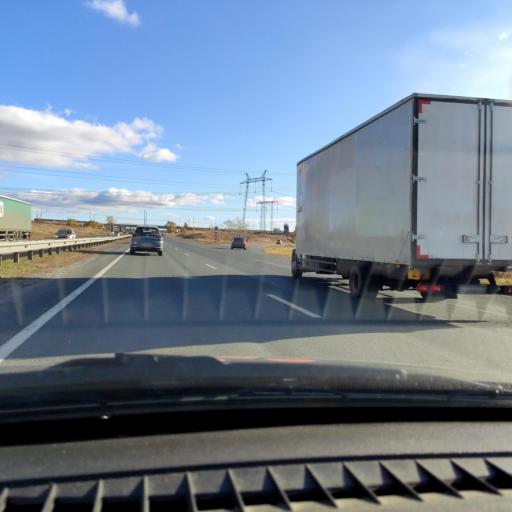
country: RU
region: Samara
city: Zhigulevsk
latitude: 53.5212
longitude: 49.5306
